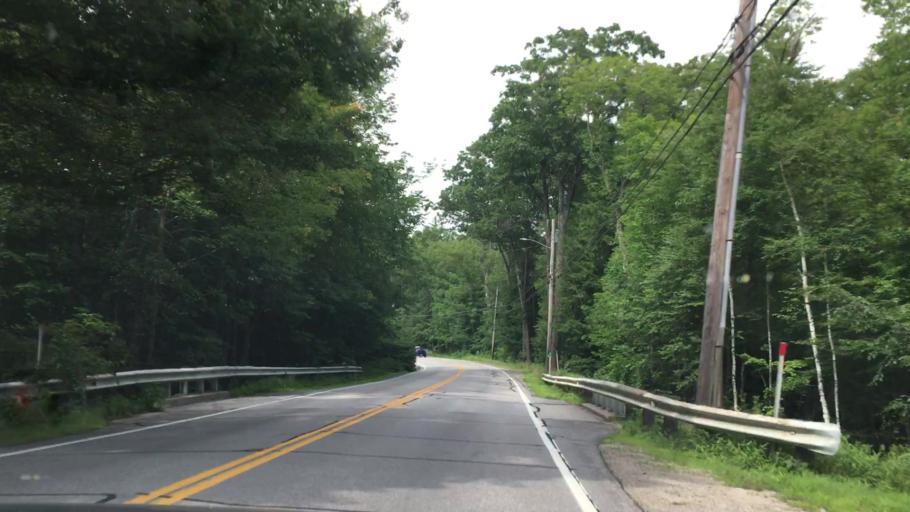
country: US
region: New Hampshire
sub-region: Hillsborough County
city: Antrim
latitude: 43.0354
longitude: -71.9359
